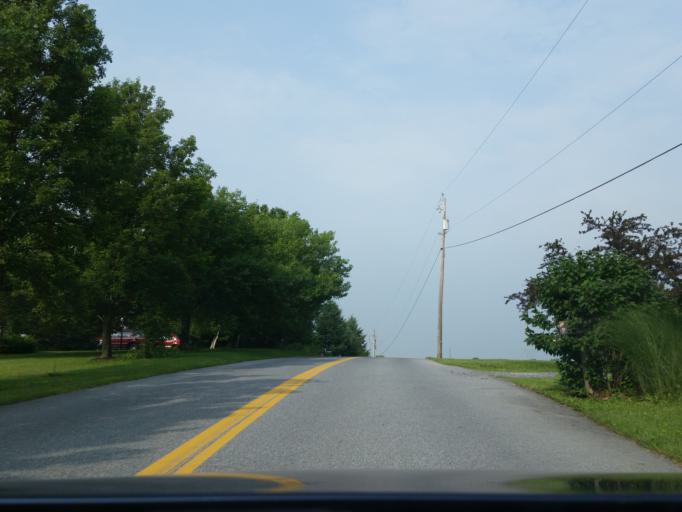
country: US
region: Pennsylvania
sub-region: Lebanon County
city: Palmyra
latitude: 40.3989
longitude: -76.6183
